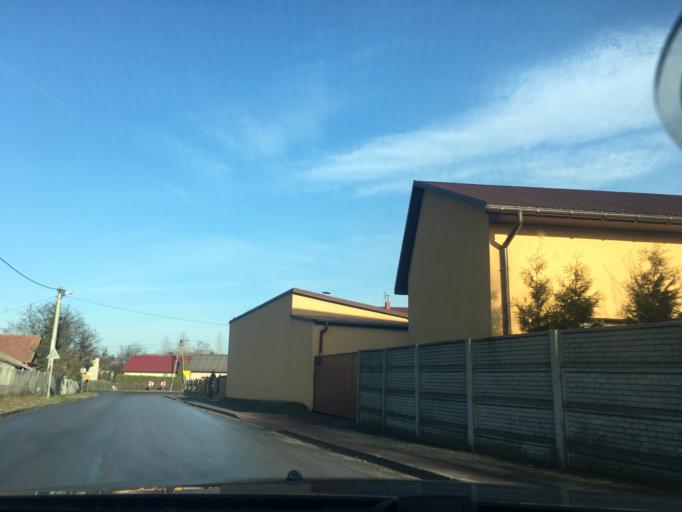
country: PL
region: Swietokrzyskie
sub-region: Powiat jedrzejowski
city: Jedrzejow
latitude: 50.6351
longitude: 20.3132
